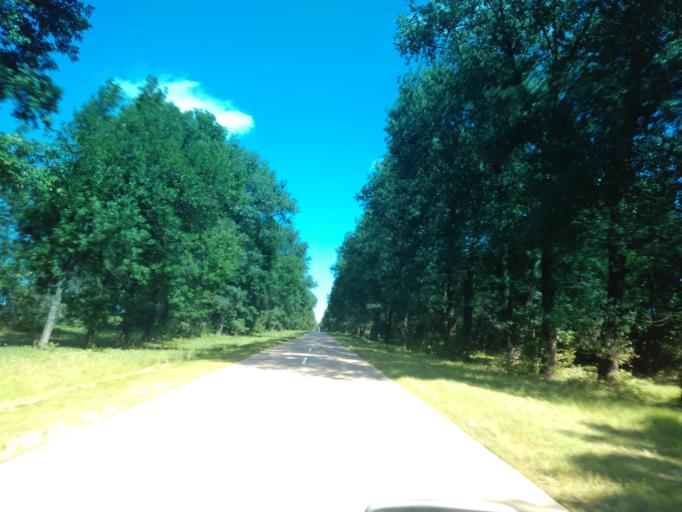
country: BY
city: Fanipol
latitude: 53.6592
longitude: 27.3231
